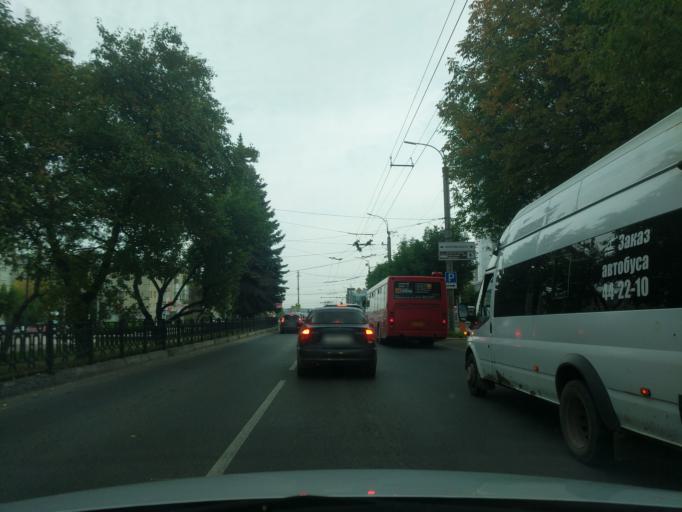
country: RU
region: Kirov
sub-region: Kirovo-Chepetskiy Rayon
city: Kirov
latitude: 58.5948
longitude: 49.6578
